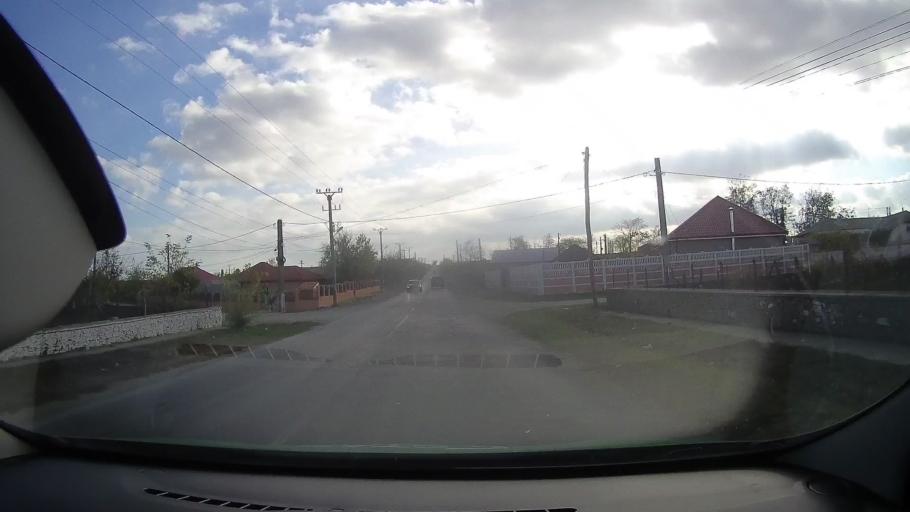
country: RO
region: Constanta
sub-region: Comuna Sacele
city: Sacele
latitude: 44.4843
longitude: 28.6458
